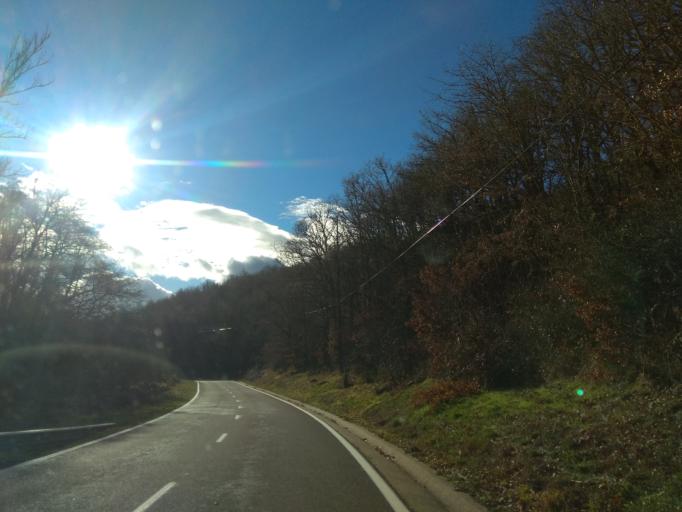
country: ES
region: Cantabria
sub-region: Provincia de Cantabria
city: San Martin de Elines
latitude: 42.8935
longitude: -3.9056
